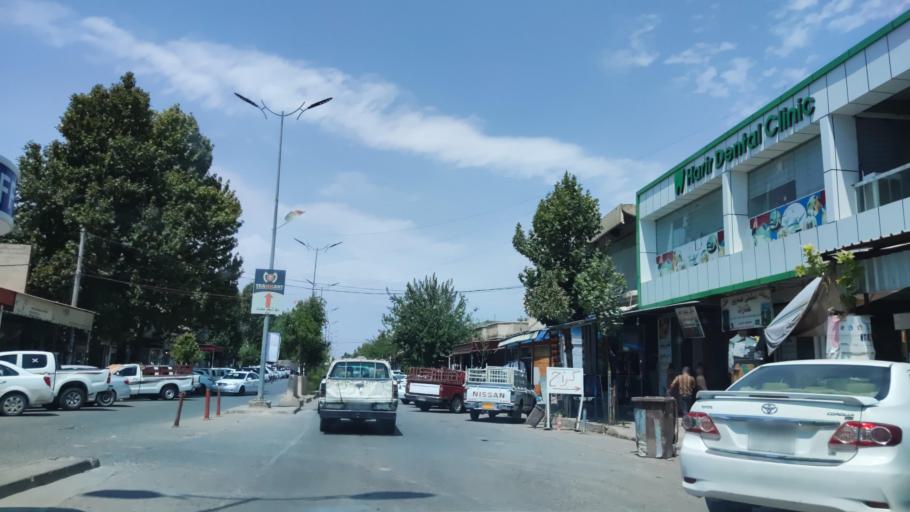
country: IQ
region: Arbil
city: Shaqlawah
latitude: 36.5521
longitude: 44.3546
